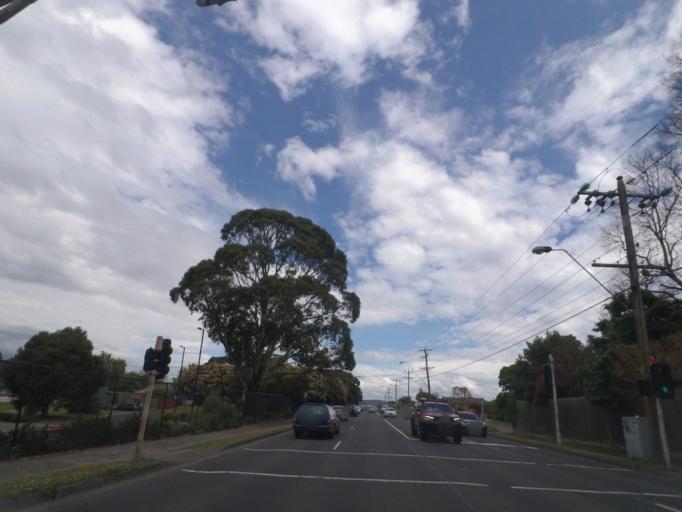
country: AU
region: Victoria
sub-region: Knox
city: Ferntree Gully
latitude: -37.8802
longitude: 145.2847
